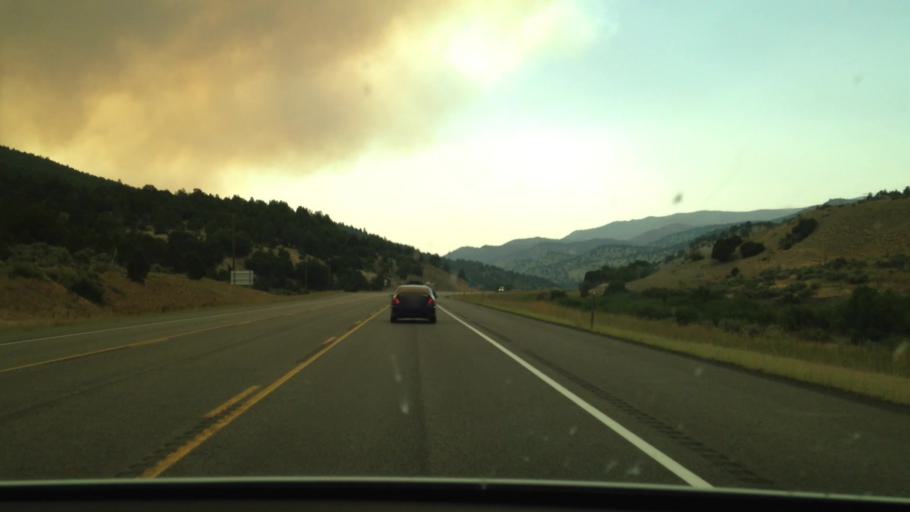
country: US
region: Utah
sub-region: Sanpete County
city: Fairview
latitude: 39.9474
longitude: -111.2114
